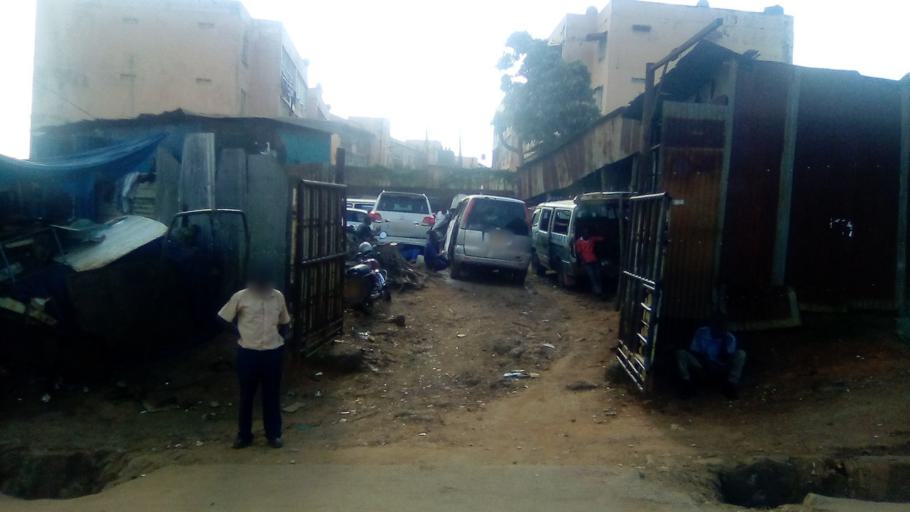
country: UG
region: Central Region
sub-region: Kampala District
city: Kampala
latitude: 0.3113
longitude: 32.5690
